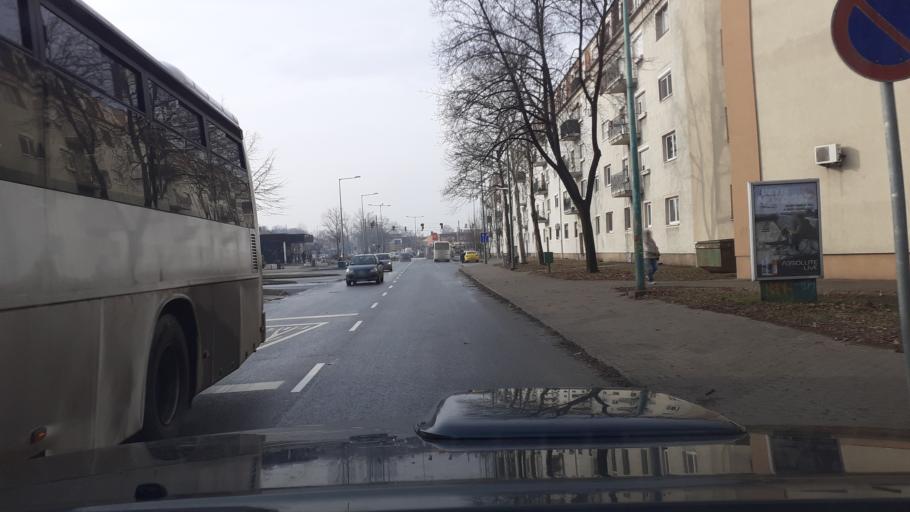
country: HU
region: Fejer
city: Dunaujvaros
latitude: 46.9585
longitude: 18.9384
